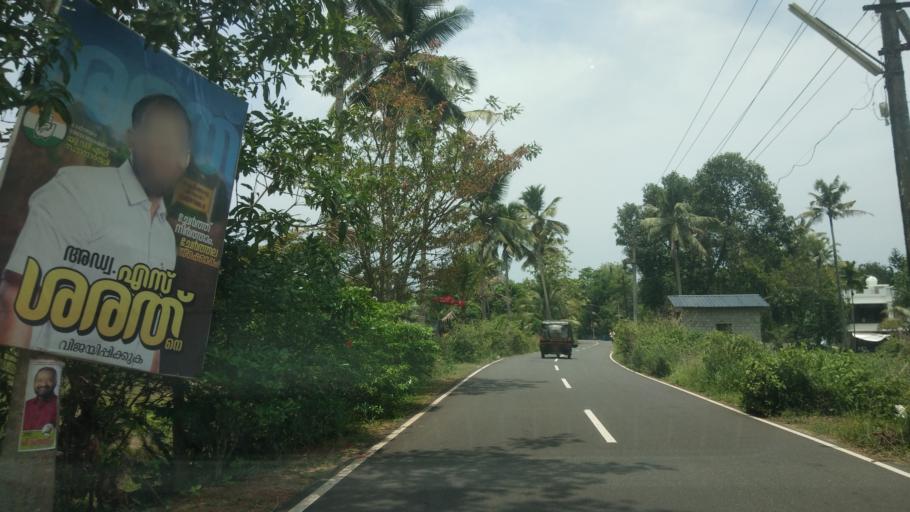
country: IN
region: Kerala
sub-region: Alappuzha
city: Shertallai
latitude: 9.6568
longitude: 76.3261
